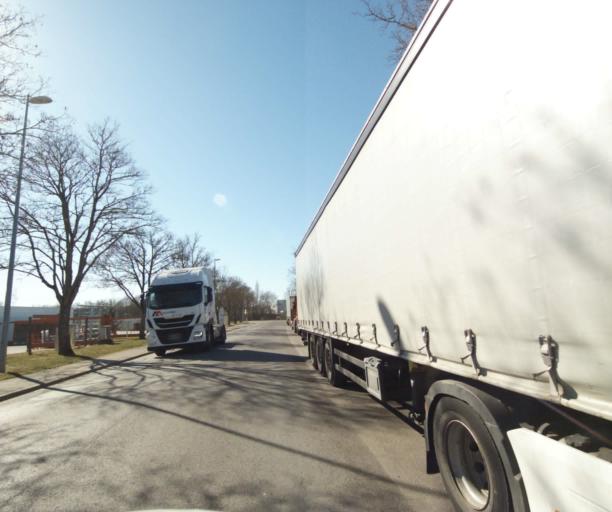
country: FR
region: Lorraine
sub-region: Departement de Meurthe-et-Moselle
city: Fleville-devant-Nancy
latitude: 48.6128
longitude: 6.1920
